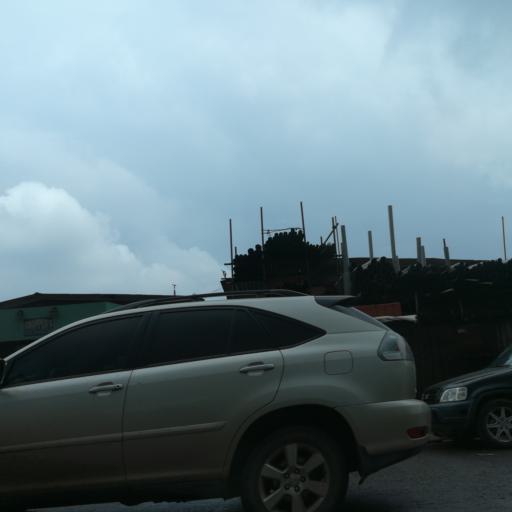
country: NG
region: Lagos
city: Agege
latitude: 6.5993
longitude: 3.2939
